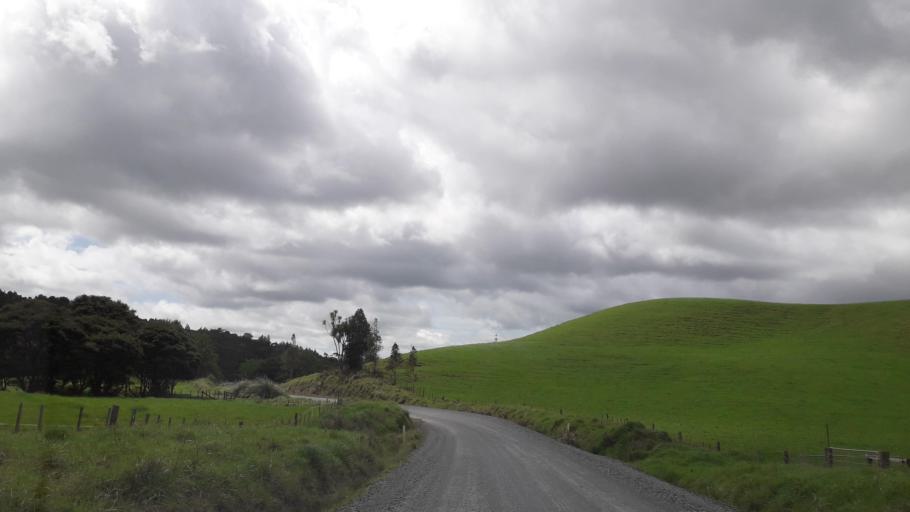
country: NZ
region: Northland
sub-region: Far North District
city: Kaitaia
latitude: -35.1734
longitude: 173.3295
